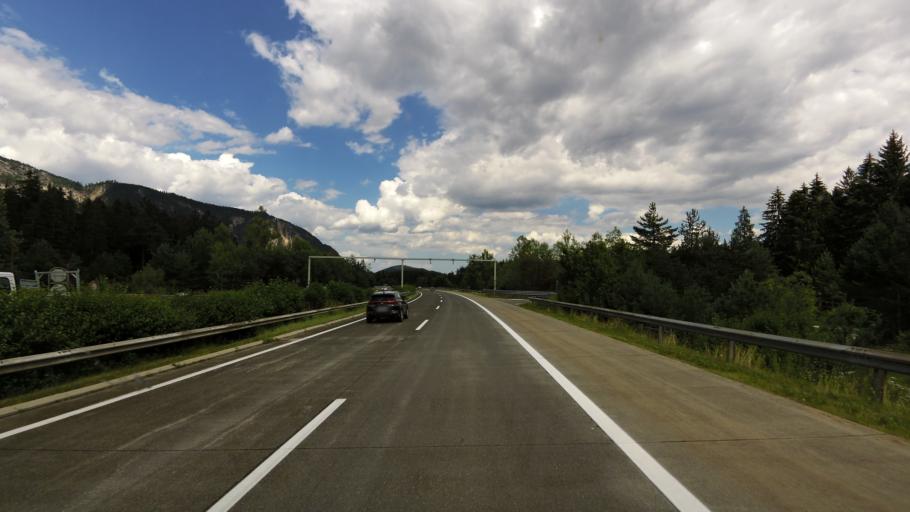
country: AT
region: Carinthia
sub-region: Politischer Bezirk Villach Land
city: Arnoldstein
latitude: 46.5578
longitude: 13.7586
